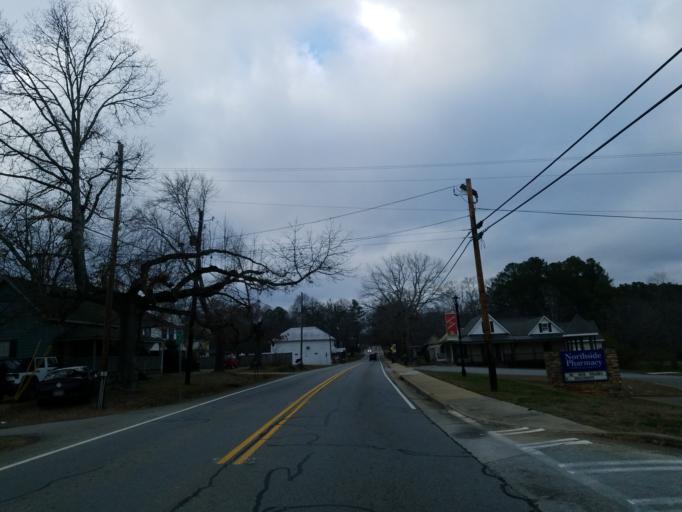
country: US
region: Georgia
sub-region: Cherokee County
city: Canton
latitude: 34.3148
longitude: -84.5501
